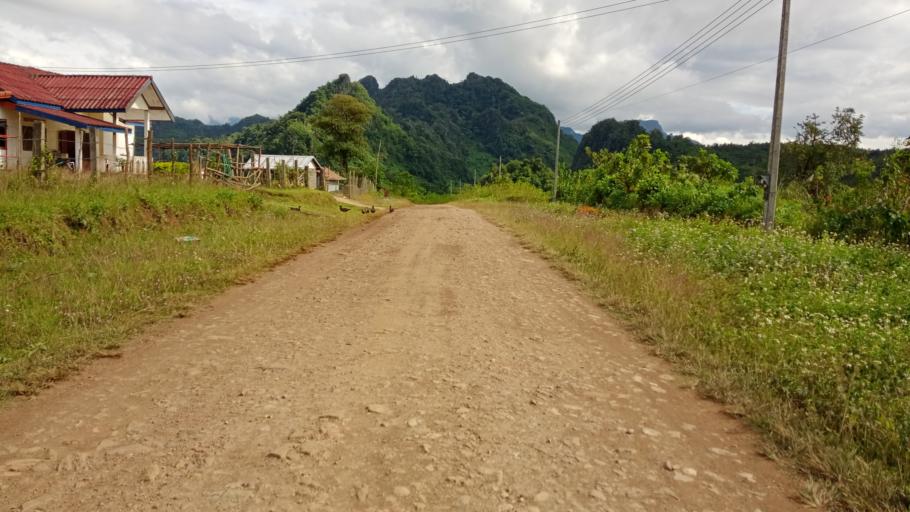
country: LA
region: Xiangkhoang
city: Phonsavan
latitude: 19.1055
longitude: 102.9302
